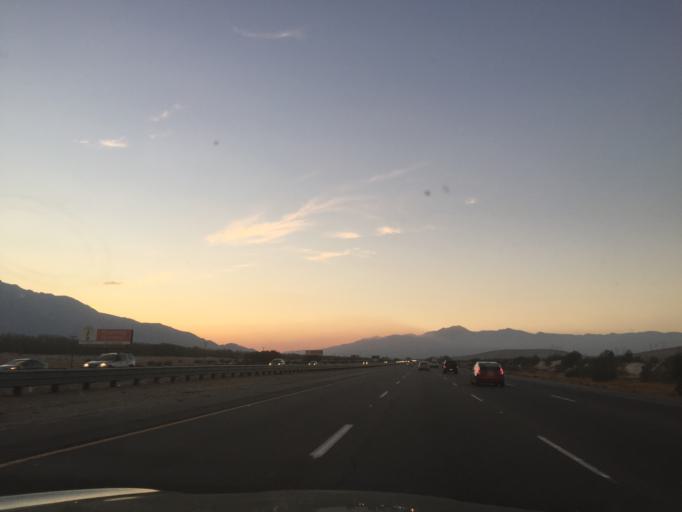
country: US
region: California
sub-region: Riverside County
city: Thousand Palms
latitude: 33.8300
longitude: -116.4254
